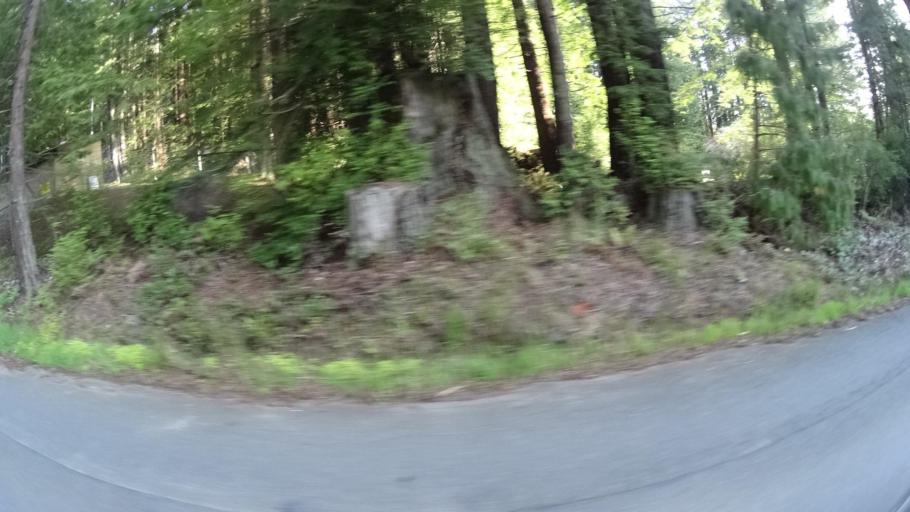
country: US
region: California
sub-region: Humboldt County
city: Myrtletown
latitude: 40.7722
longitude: -124.1157
